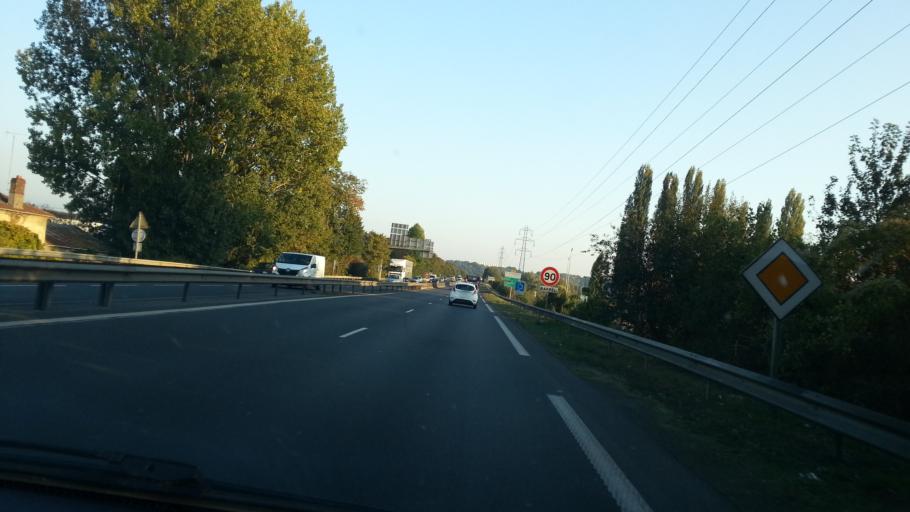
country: FR
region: Picardie
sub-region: Departement de l'Oise
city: Nogent-sur-Oise
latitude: 49.2822
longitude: 2.4783
